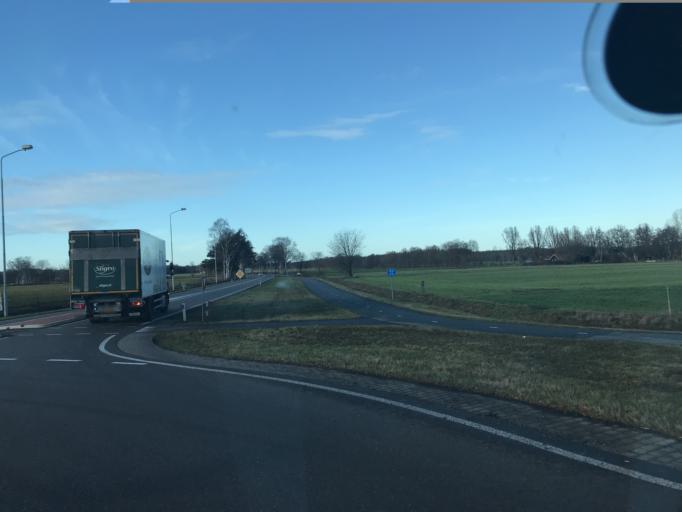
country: NL
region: Gelderland
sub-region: Gemeente Barneveld
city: Garderen
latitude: 52.2747
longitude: 5.7275
